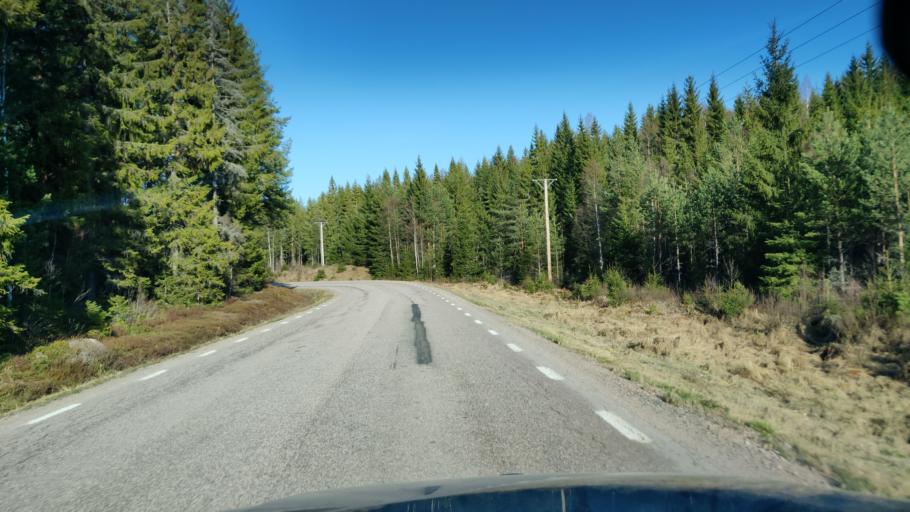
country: SE
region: Vaermland
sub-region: Munkfors Kommun
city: Munkfors
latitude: 59.9816
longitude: 13.3703
